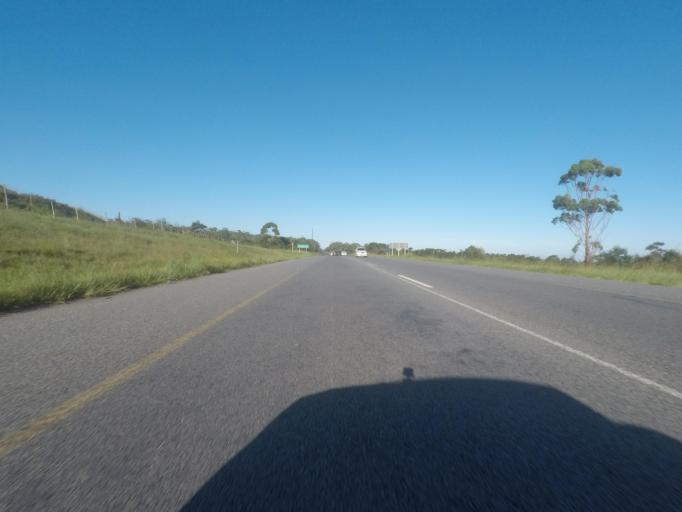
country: ZA
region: Eastern Cape
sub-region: Buffalo City Metropolitan Municipality
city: East London
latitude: -33.0491
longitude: 27.8173
